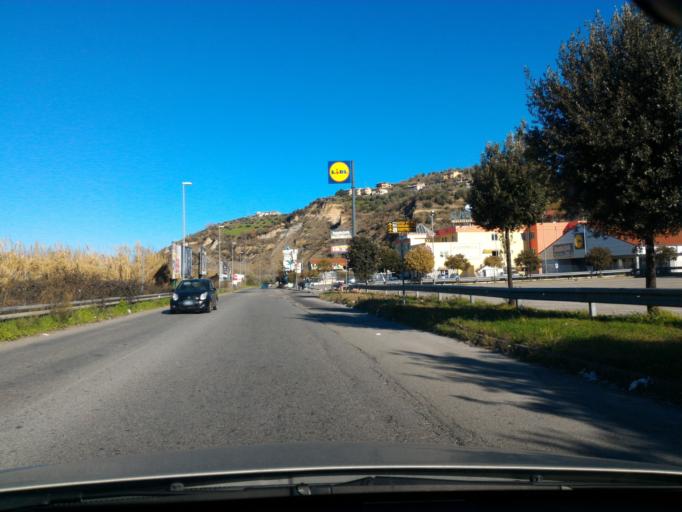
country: IT
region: Calabria
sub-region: Provincia di Cosenza
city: Cosenza
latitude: 39.3138
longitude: 16.2626
